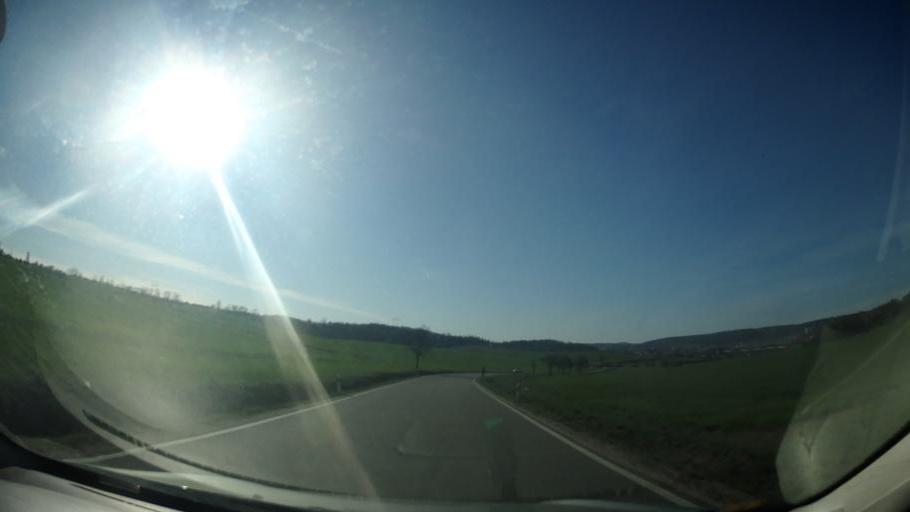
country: CZ
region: South Moravian
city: Moravany
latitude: 49.1503
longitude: 16.5618
